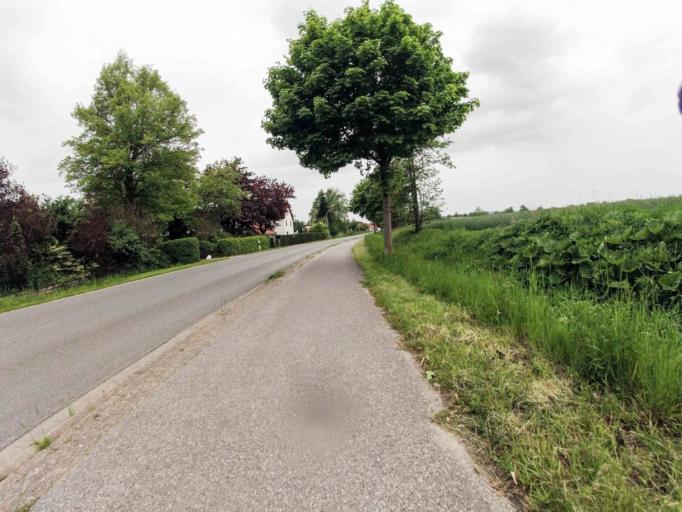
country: DE
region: Lower Saxony
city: Melle
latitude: 52.2435
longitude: 8.2903
